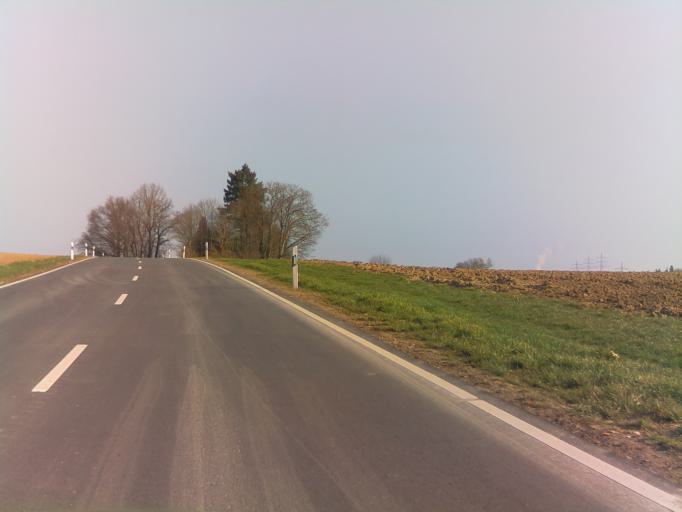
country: DE
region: Baden-Wuerttemberg
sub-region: Regierungsbezirk Stuttgart
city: Eberdingen
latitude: 48.8582
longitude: 8.9844
